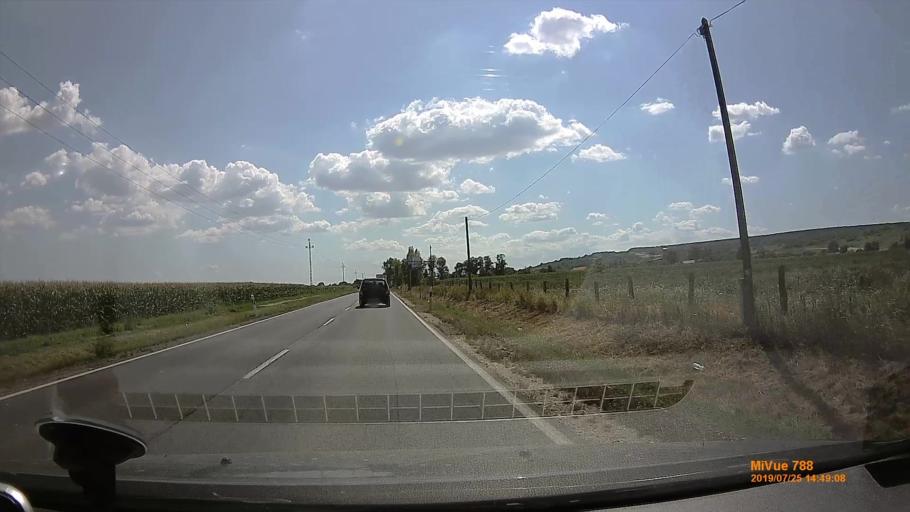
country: HU
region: Borsod-Abauj-Zemplen
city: Aszalo
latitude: 48.2309
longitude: 20.9598
